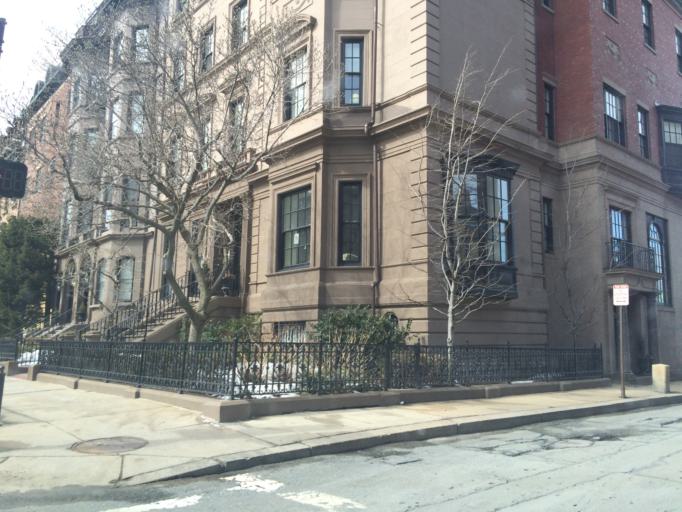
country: US
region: Massachusetts
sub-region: Suffolk County
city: Boston
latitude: 42.3549
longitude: -71.0747
